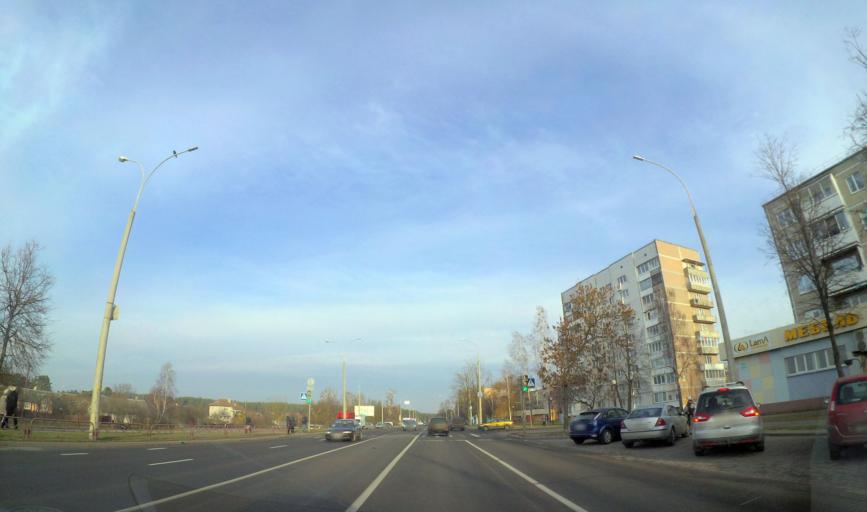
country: BY
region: Grodnenskaya
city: Hrodna
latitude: 53.6692
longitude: 23.7904
